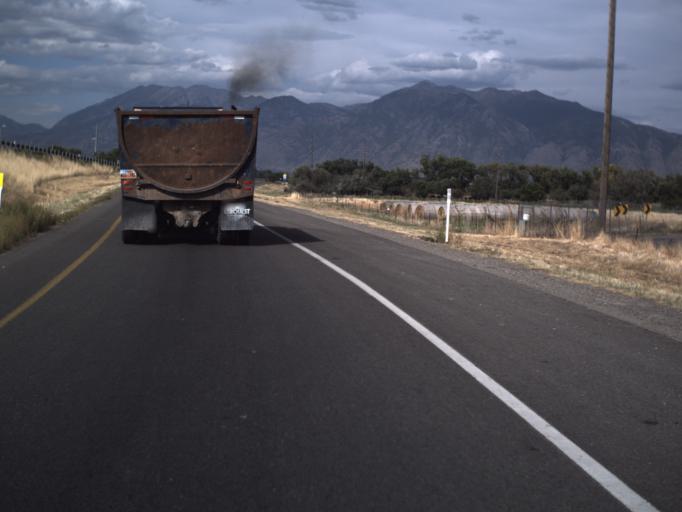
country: US
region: Utah
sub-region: Utah County
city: Payson
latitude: 40.0555
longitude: -111.7313
